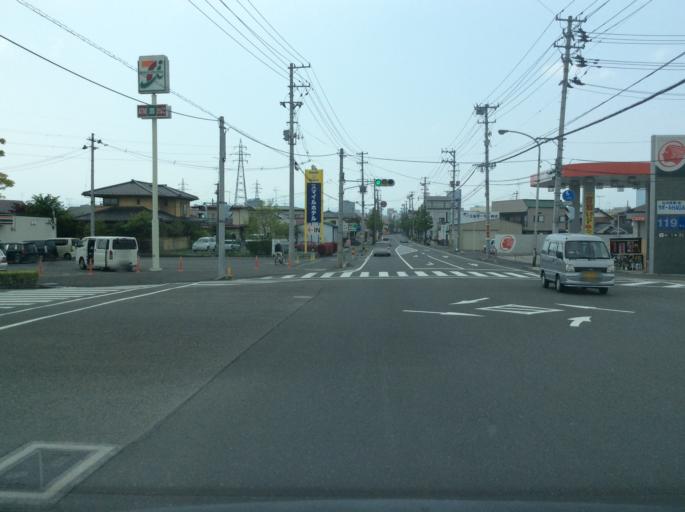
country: JP
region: Fukushima
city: Koriyama
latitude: 37.3877
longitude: 140.3996
